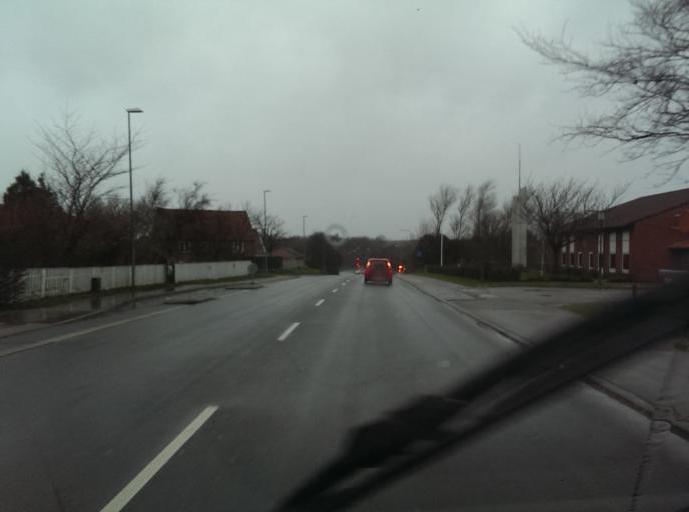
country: DK
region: South Denmark
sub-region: Esbjerg Kommune
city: Esbjerg
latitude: 55.4921
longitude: 8.4537
